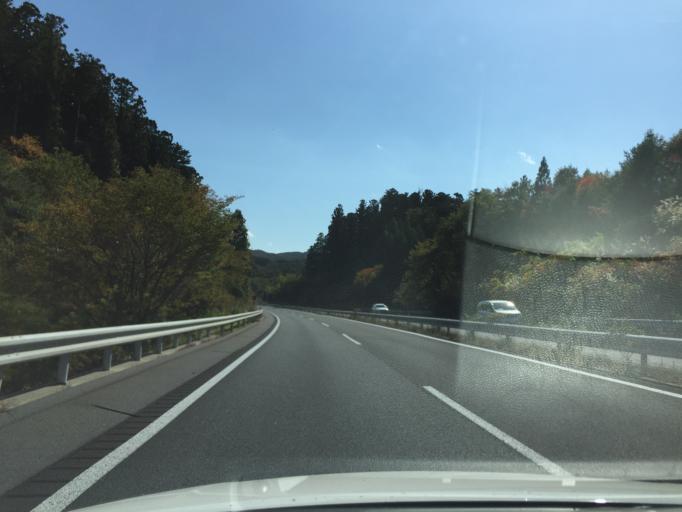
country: JP
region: Fukushima
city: Ishikawa
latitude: 37.2127
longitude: 140.6915
